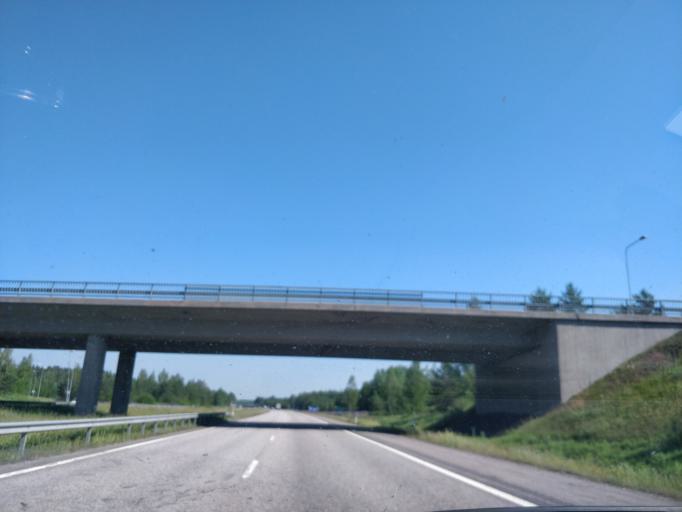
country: FI
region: Uusimaa
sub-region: Helsinki
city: Hyvinge
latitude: 60.6195
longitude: 24.8088
